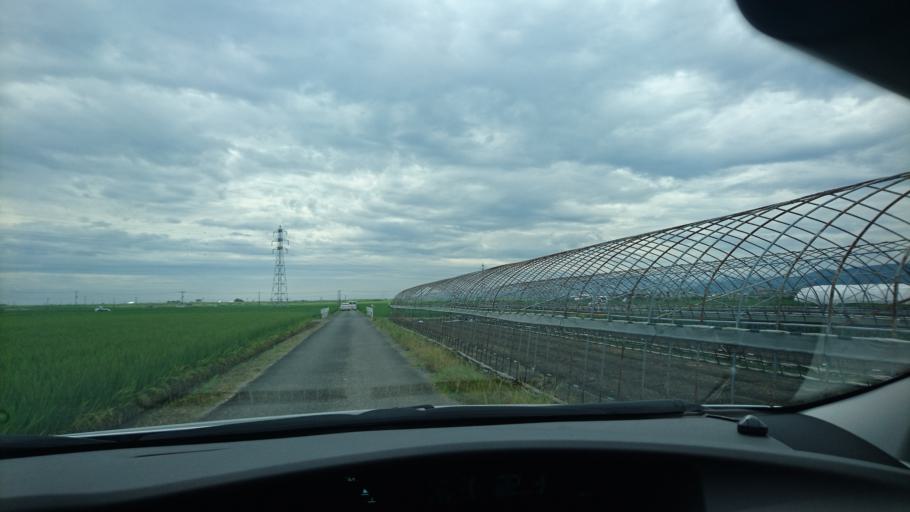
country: JP
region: Saga Prefecture
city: Takeocho-takeo
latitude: 33.2131
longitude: 130.1257
